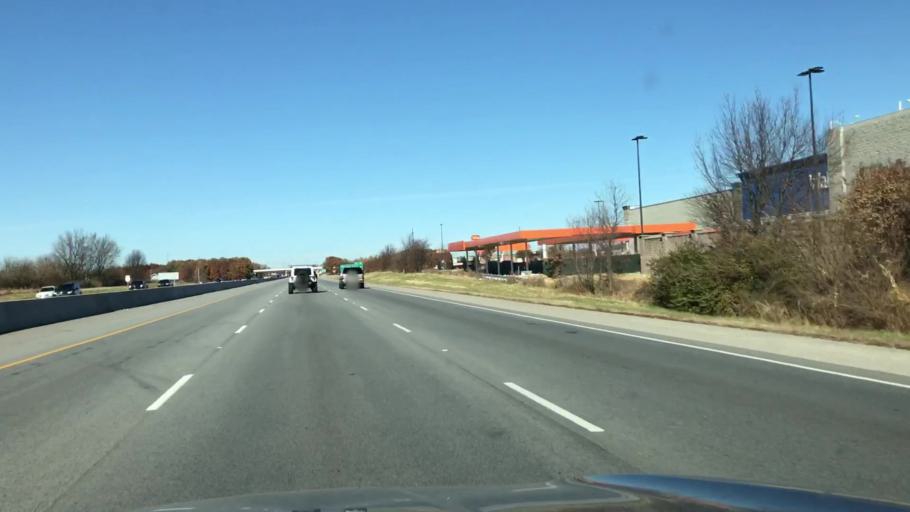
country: US
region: Arkansas
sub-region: Benton County
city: Lowell
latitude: 36.2785
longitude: -94.1520
